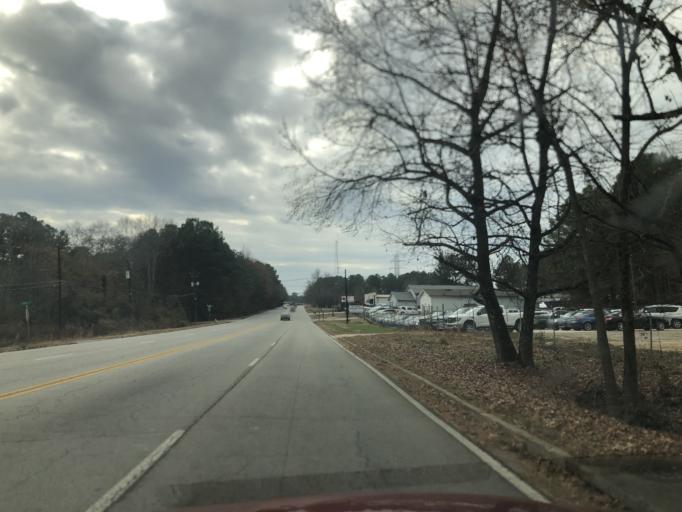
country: US
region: Georgia
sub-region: Clayton County
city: Lake City
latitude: 33.6066
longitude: -84.3310
